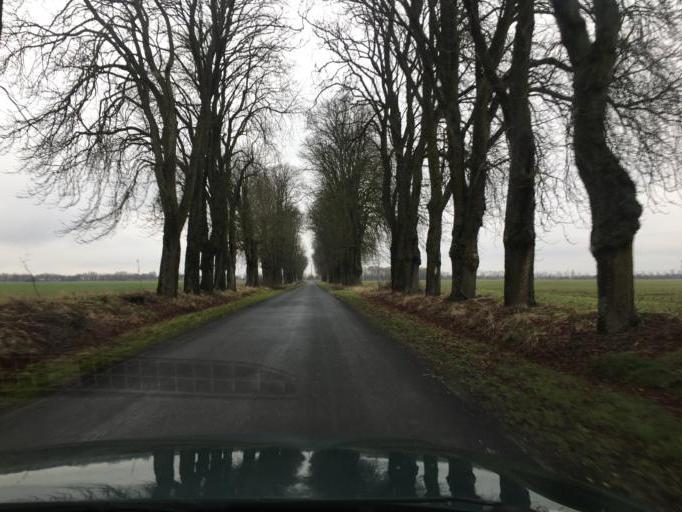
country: FR
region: Centre
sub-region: Departement du Loiret
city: Chevilly
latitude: 48.0228
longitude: 1.8516
